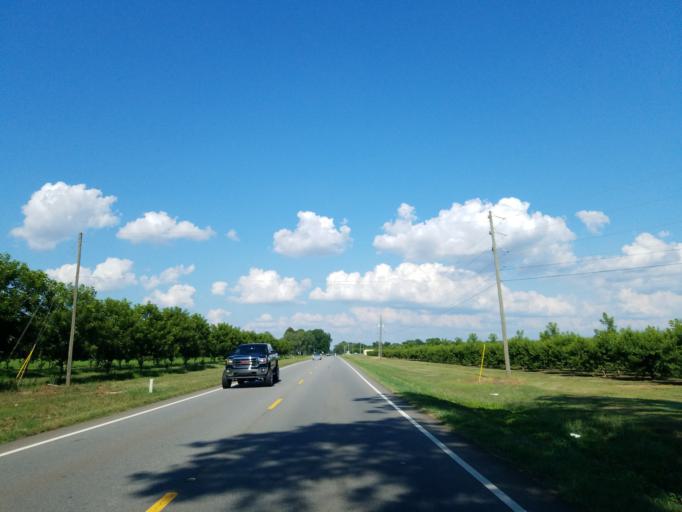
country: US
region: Georgia
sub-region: Peach County
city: Fort Valley
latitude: 32.5539
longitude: -83.8059
